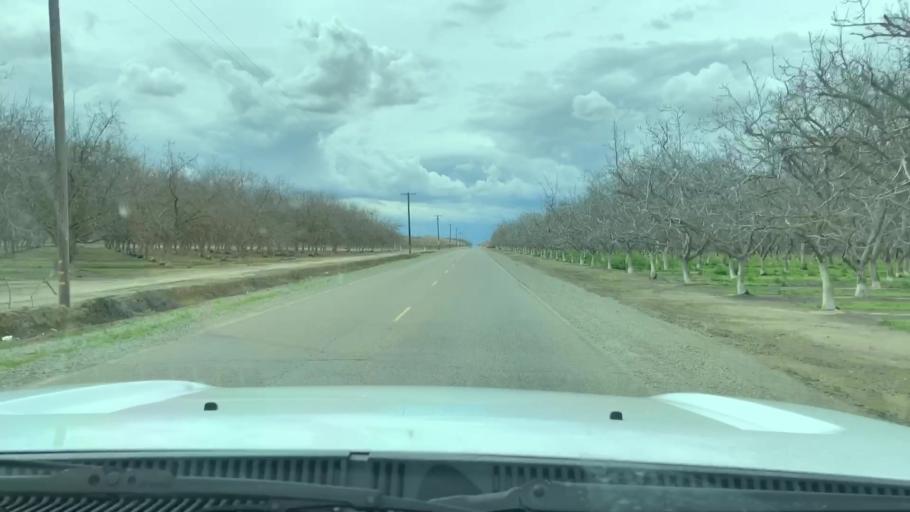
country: US
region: California
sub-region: Fresno County
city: Caruthers
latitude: 36.4894
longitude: -119.7595
